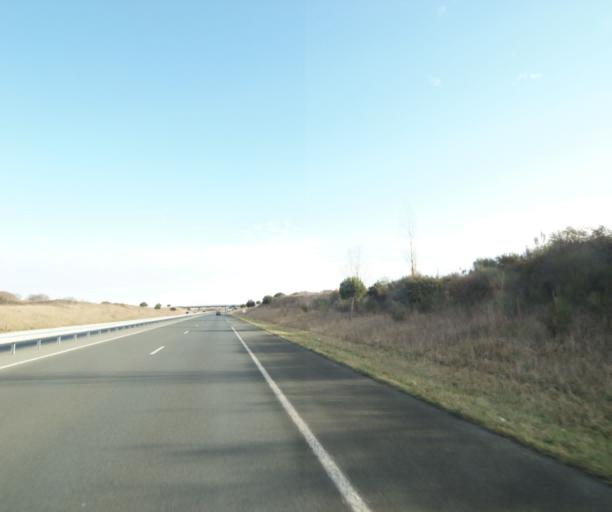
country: FR
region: Poitou-Charentes
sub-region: Departement de la Charente-Maritime
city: Saint-Romain-de-Benet
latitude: 45.6911
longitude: -0.8303
